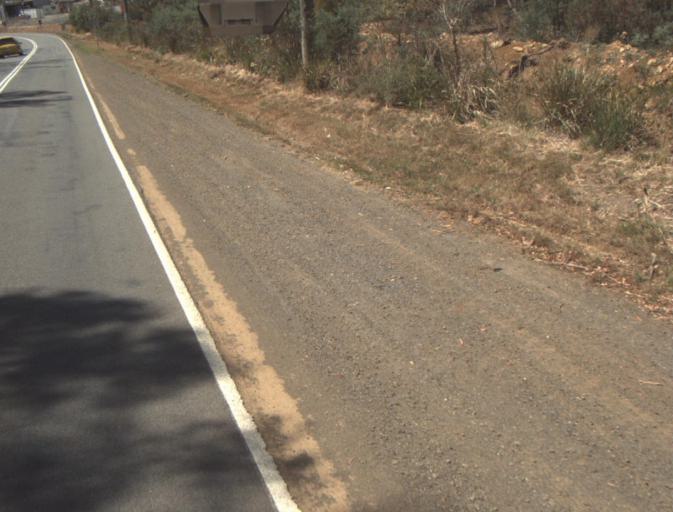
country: AU
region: Tasmania
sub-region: Launceston
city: Mayfield
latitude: -41.3660
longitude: 147.1432
